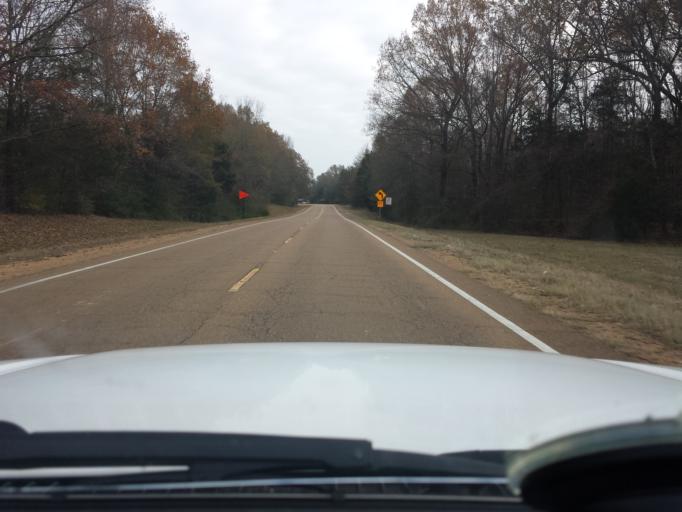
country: US
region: Mississippi
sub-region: Yazoo County
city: Yazoo City
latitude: 32.8065
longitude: -90.2340
